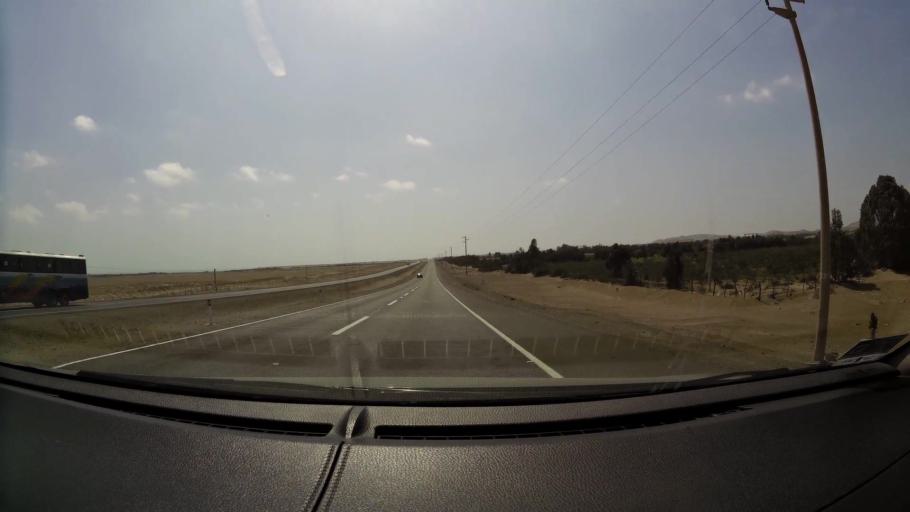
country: PE
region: Lima
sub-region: Huaura
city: Huacho
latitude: -11.2219
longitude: -77.5493
